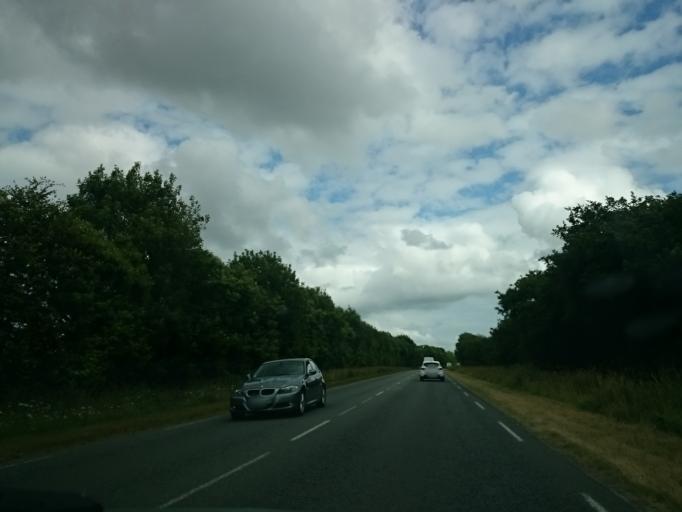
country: FR
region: Brittany
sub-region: Departement du Finistere
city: Gouesnou
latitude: 48.4371
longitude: -4.4502
